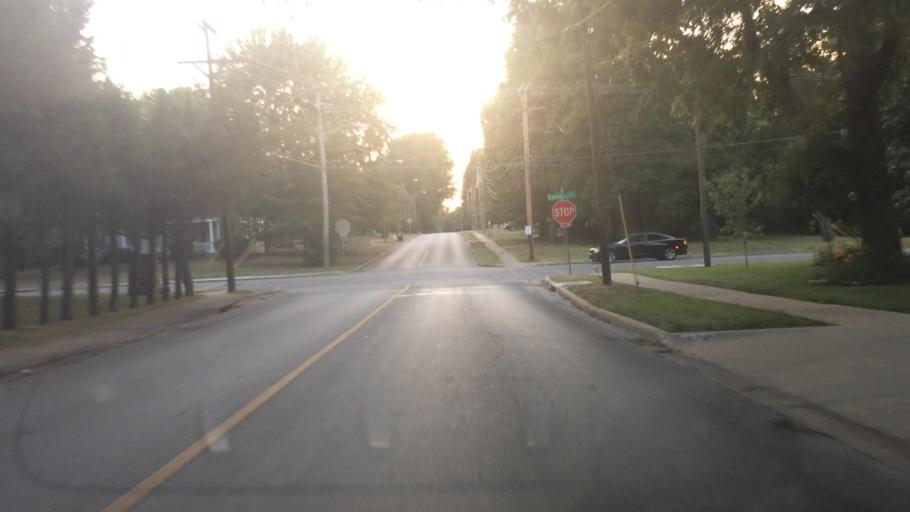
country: US
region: Missouri
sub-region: Greene County
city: Springfield
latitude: 37.1854
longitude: -93.2707
